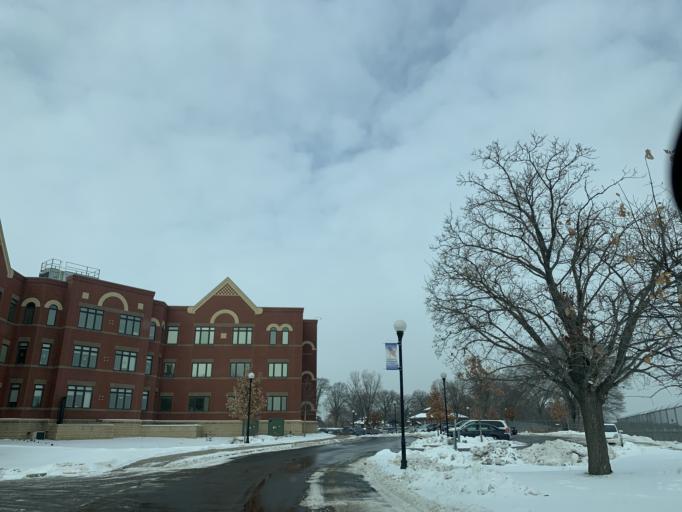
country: US
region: Minnesota
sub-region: Dakota County
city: Mendota Heights
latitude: 44.9137
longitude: -93.2029
